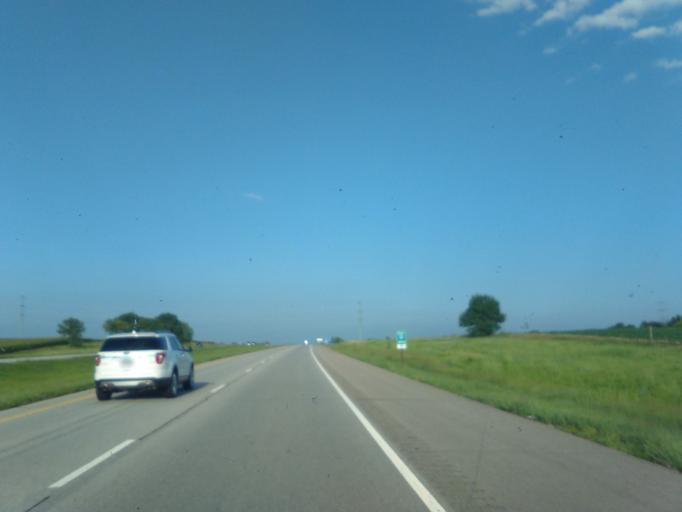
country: US
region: Nebraska
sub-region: Lancaster County
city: Lincoln
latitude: 40.8213
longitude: -96.8221
